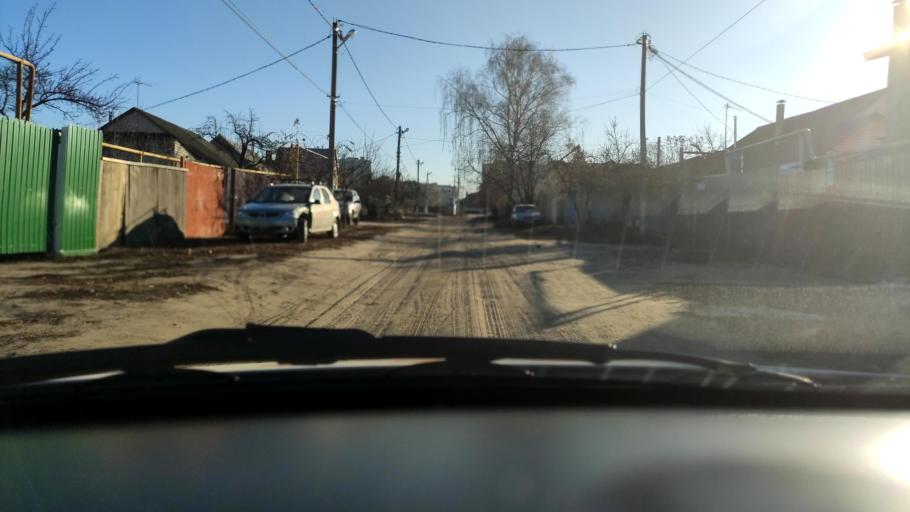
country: RU
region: Voronezj
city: Podgornoye
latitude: 51.7295
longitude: 39.1566
